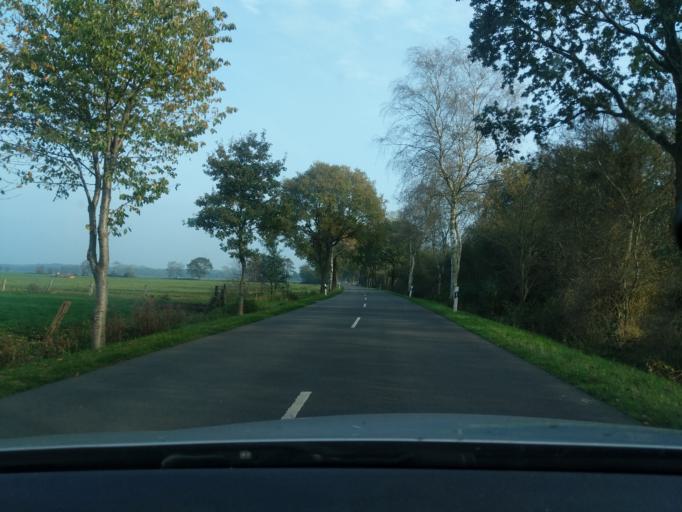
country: DE
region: Lower Saxony
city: Stinstedt
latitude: 53.6487
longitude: 8.9944
